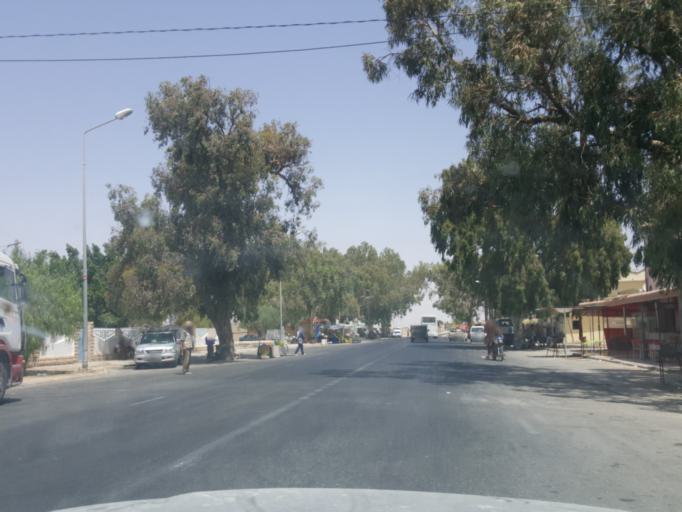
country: TN
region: Safaqis
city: Skhira
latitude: 34.1048
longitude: 9.9833
